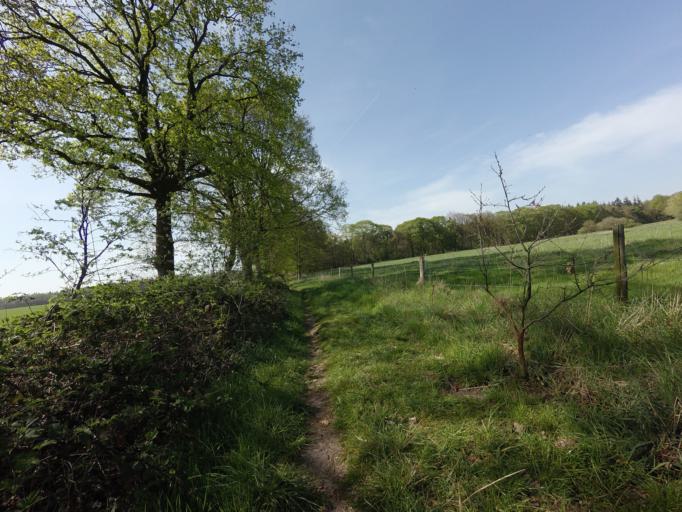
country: NL
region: North Brabant
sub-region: Gemeente Goirle
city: Goirle
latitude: 51.4768
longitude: 5.0036
